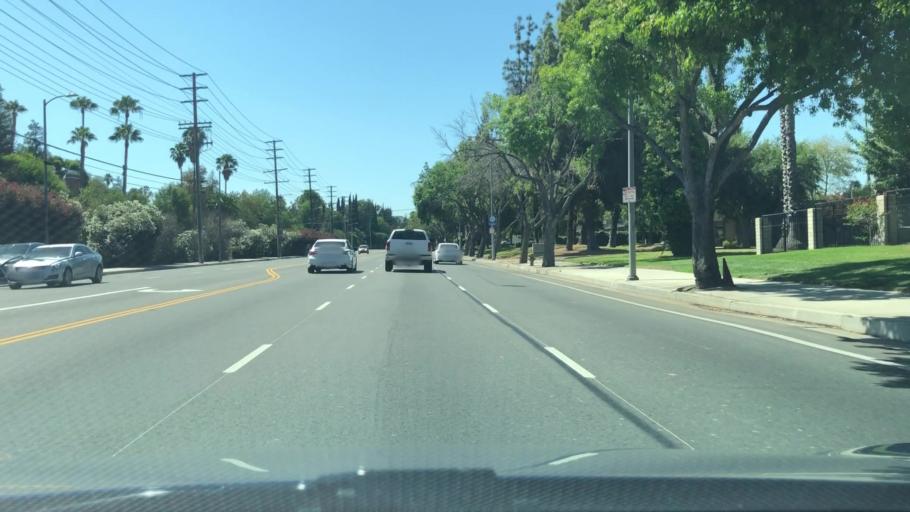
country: US
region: California
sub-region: Los Angeles County
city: Woodland Hills
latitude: 34.1772
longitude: -118.5899
